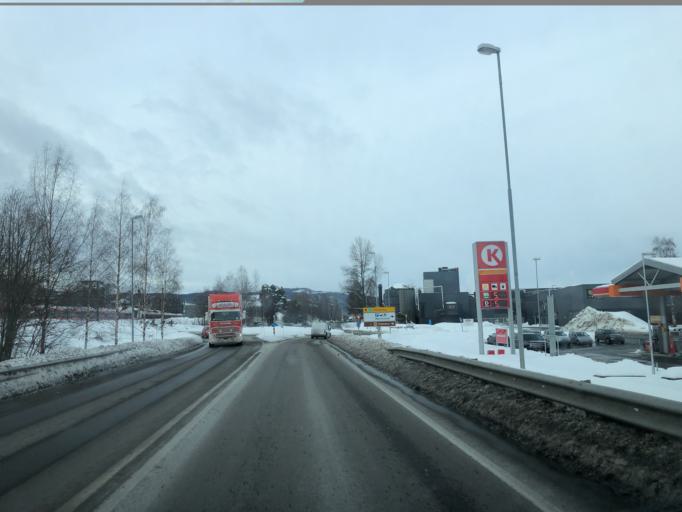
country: NO
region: Oppland
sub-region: Gjovik
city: Gjovik
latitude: 60.7946
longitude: 10.6970
